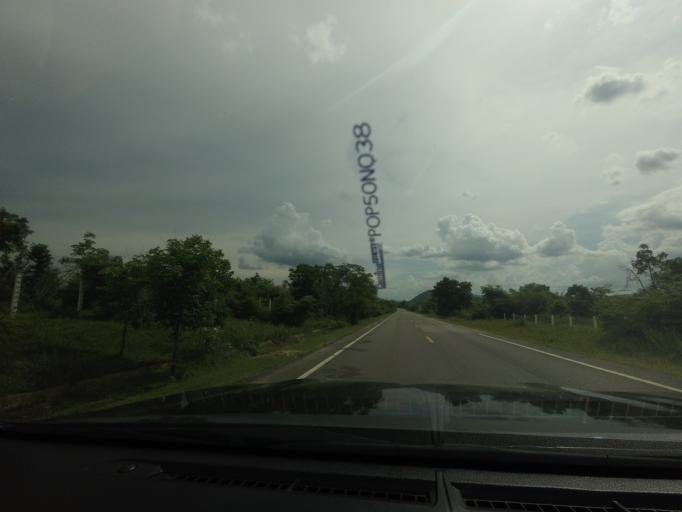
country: TH
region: Kanchanaburi
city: Bo Phloi
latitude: 14.1616
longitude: 99.4296
